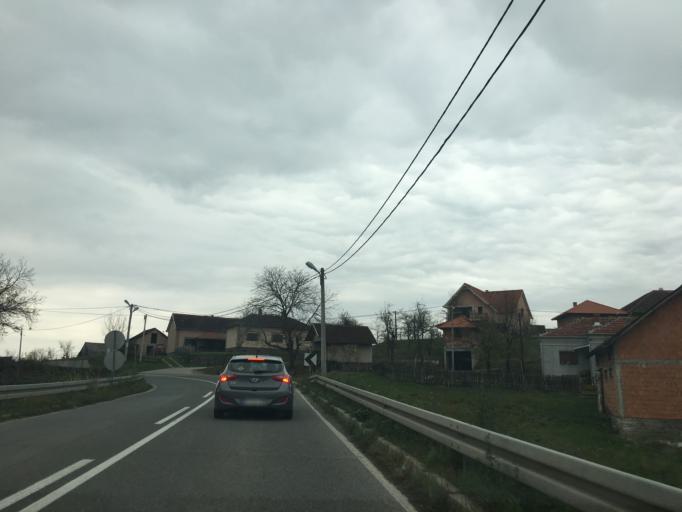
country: RS
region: Central Serbia
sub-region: Raski Okrug
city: Kraljevo
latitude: 43.7153
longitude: 20.7965
